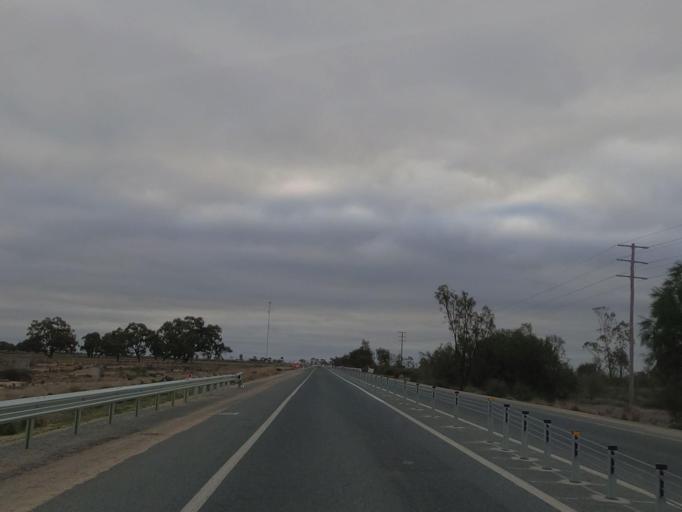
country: AU
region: Victoria
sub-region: Swan Hill
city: Swan Hill
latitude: -35.5337
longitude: 143.7431
